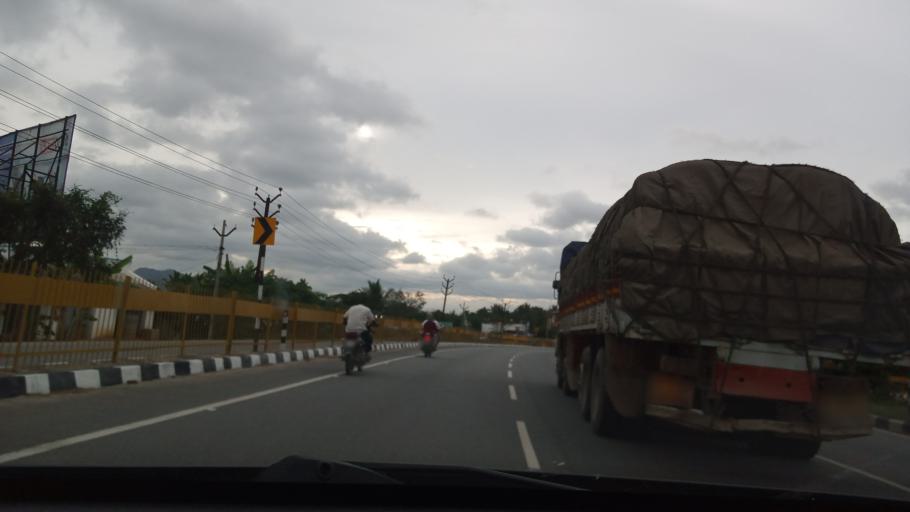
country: IN
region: Tamil Nadu
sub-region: Krishnagiri
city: Krishnagiri
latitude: 12.5342
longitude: 78.2993
